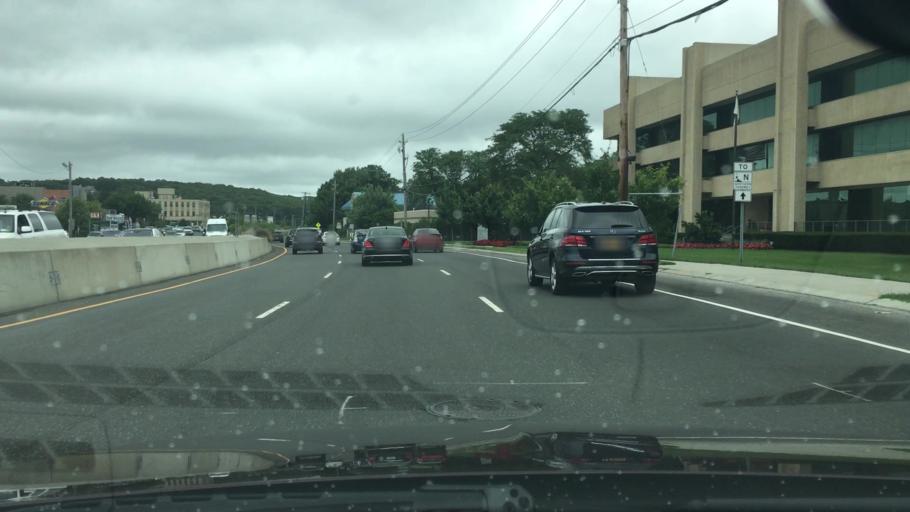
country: US
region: New York
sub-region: Suffolk County
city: Melville
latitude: 40.7889
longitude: -73.4154
